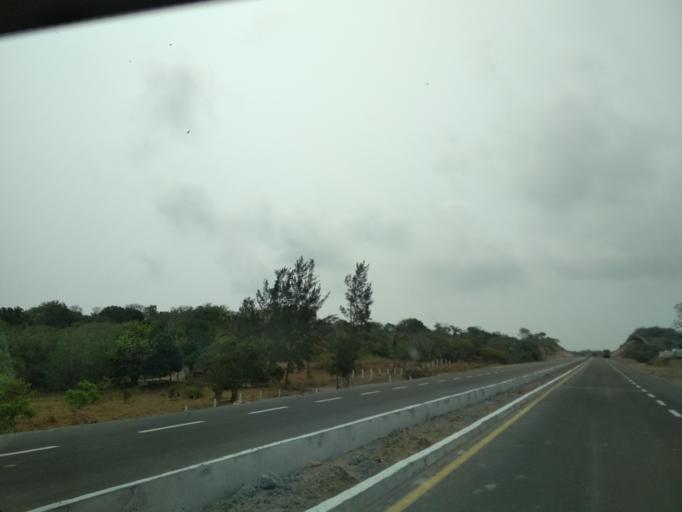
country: MX
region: Veracruz
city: Anton Lizardo
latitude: 19.0460
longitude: -95.9981
